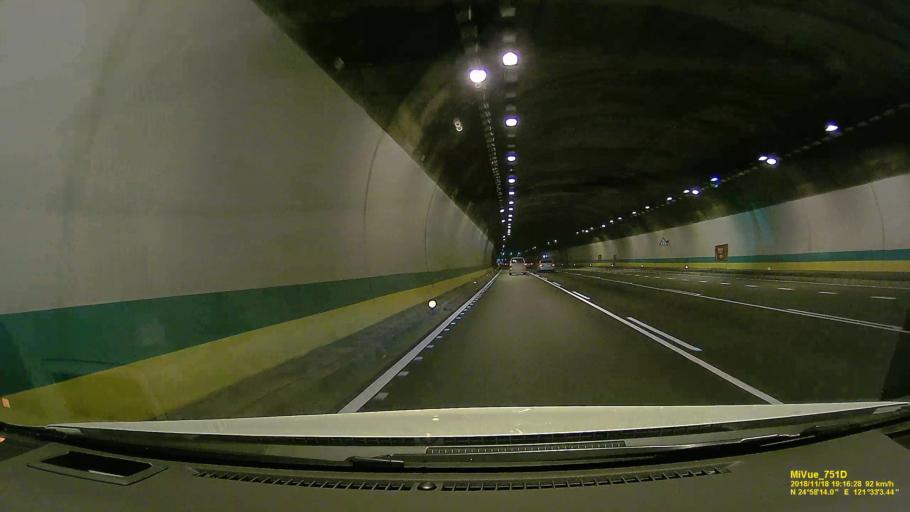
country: TW
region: Taipei
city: Taipei
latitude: 24.9703
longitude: 121.5506
